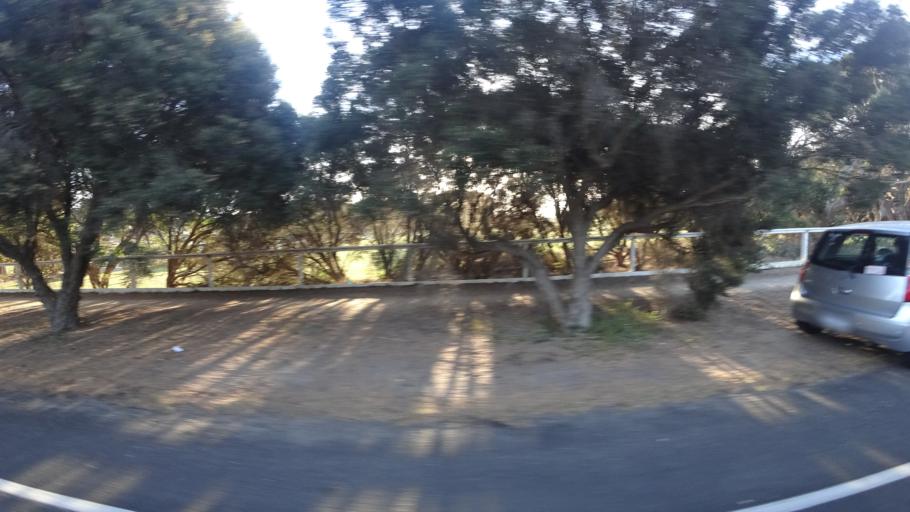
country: AU
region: Victoria
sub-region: Queenscliffe
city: Queenscliff
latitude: -38.2789
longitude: 144.6164
